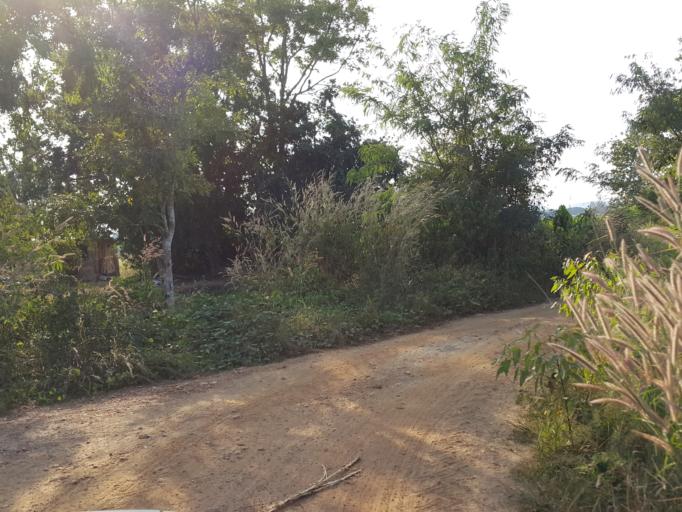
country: TH
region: Sukhothai
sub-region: Amphoe Si Satchanalai
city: Si Satchanalai
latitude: 17.4730
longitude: 99.6554
